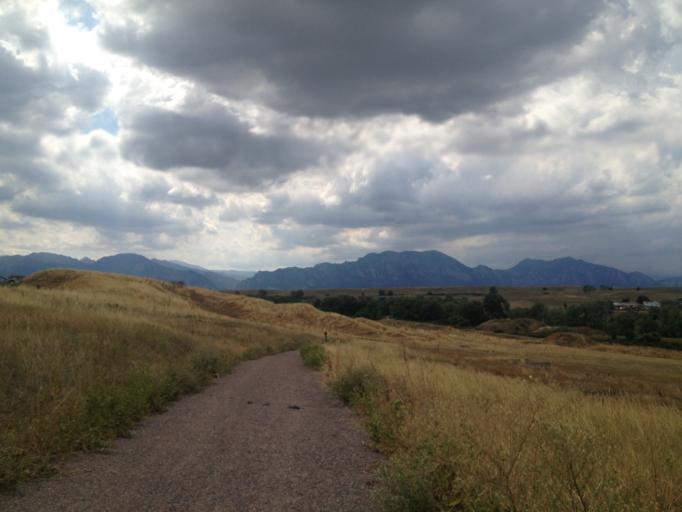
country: US
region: Colorado
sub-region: Boulder County
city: Superior
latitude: 39.9480
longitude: -105.1676
